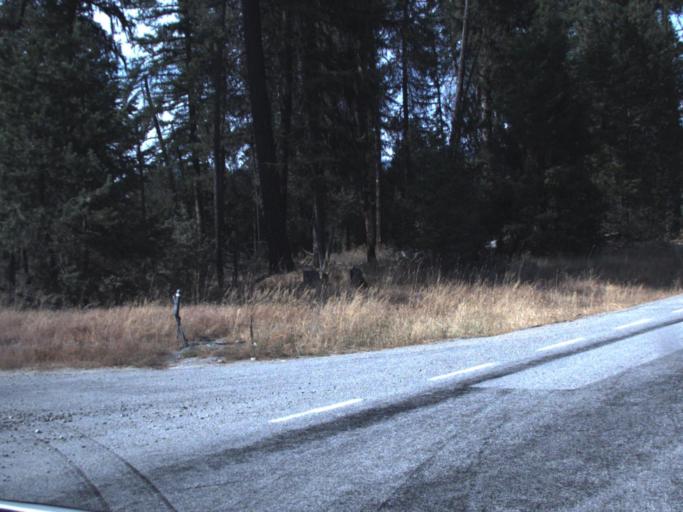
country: US
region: Washington
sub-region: Pend Oreille County
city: Newport
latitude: 48.1816
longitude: -117.3015
